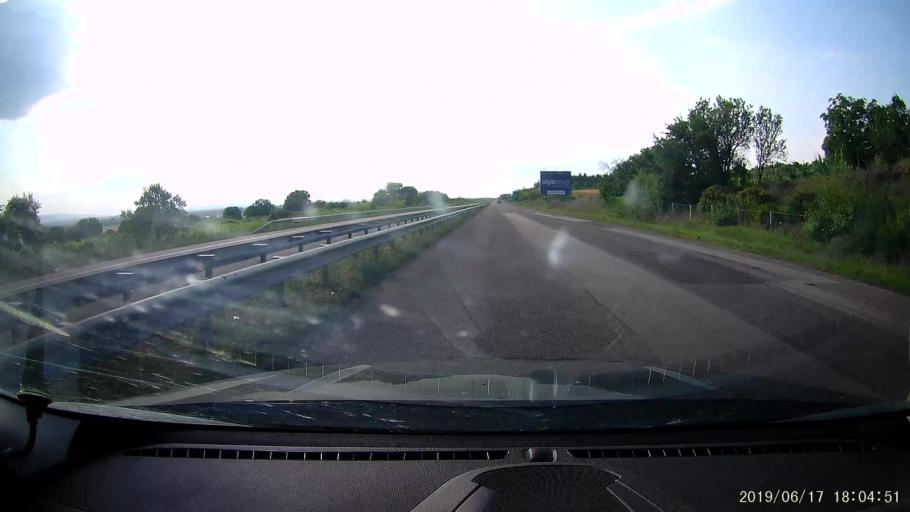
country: BG
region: Khaskovo
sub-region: Obshtina Svilengrad
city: Svilengrad
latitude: 41.7906
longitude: 26.1894
